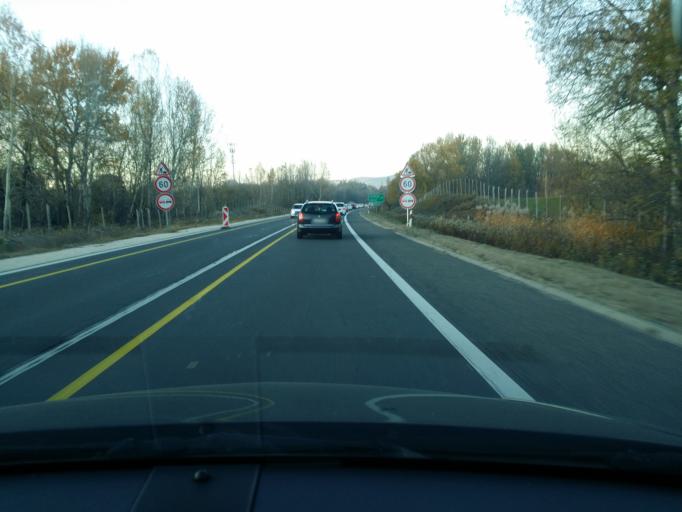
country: HU
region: Pest
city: Szod
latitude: 47.7217
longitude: 19.1575
